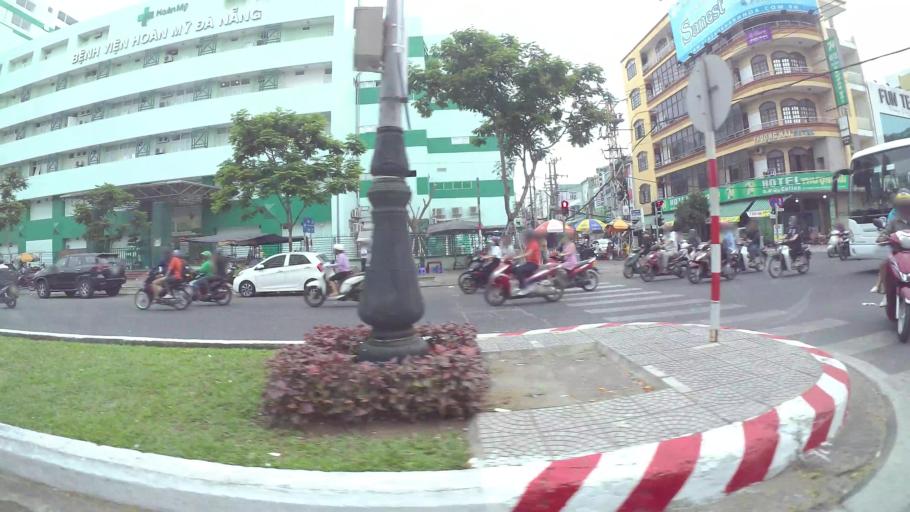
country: VN
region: Da Nang
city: Da Nang
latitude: 16.0597
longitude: 108.2095
